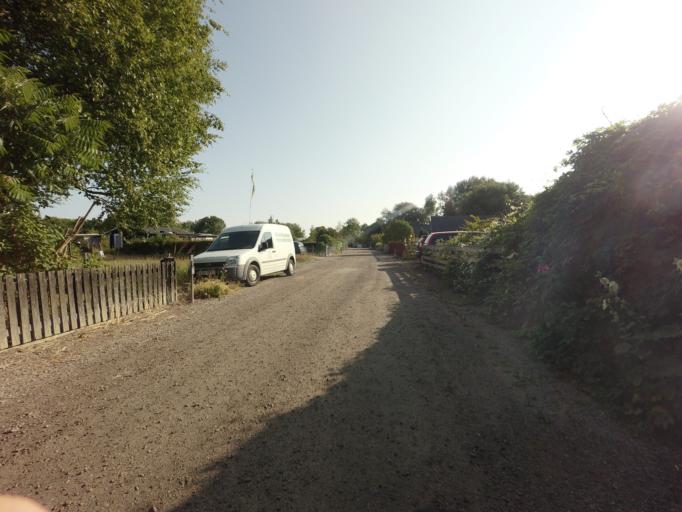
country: SE
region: Skane
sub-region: Landskrona
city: Asmundtorp
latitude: 55.8600
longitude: 12.8924
